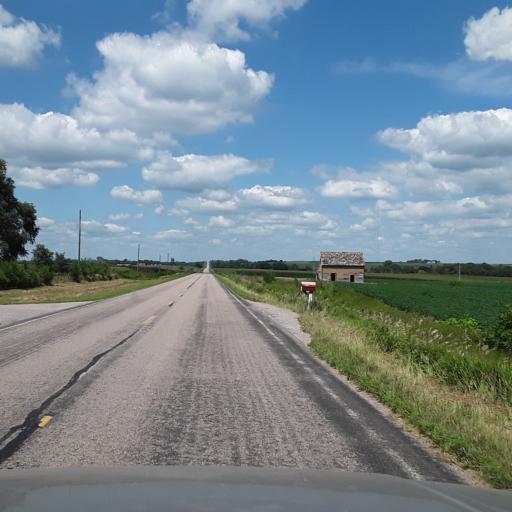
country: US
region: Nebraska
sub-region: Nance County
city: Genoa
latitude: 41.4875
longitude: -97.6957
